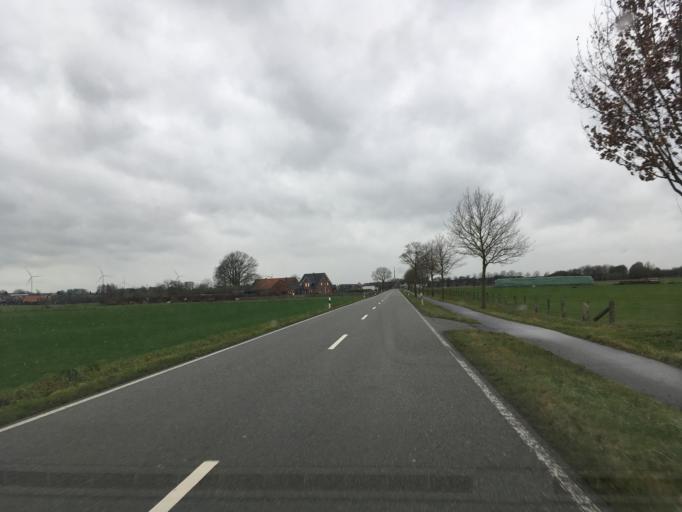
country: DE
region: North Rhine-Westphalia
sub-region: Regierungsbezirk Munster
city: Legden
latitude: 52.0401
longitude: 7.1192
